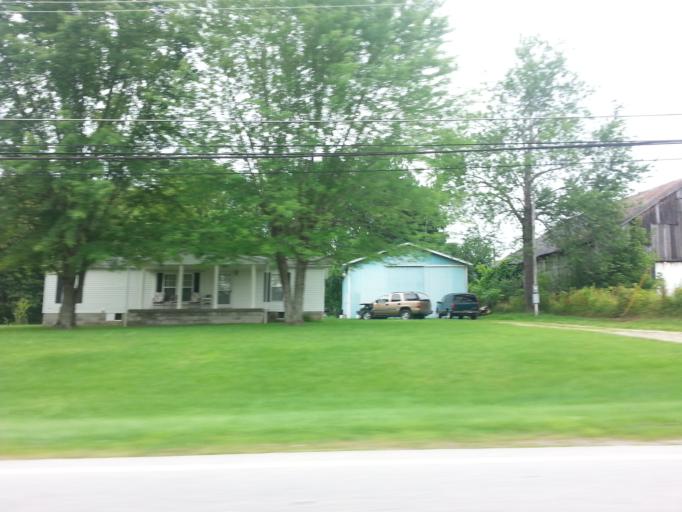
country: US
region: Ohio
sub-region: Brown County
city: Ripley
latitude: 38.7264
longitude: -83.8321
